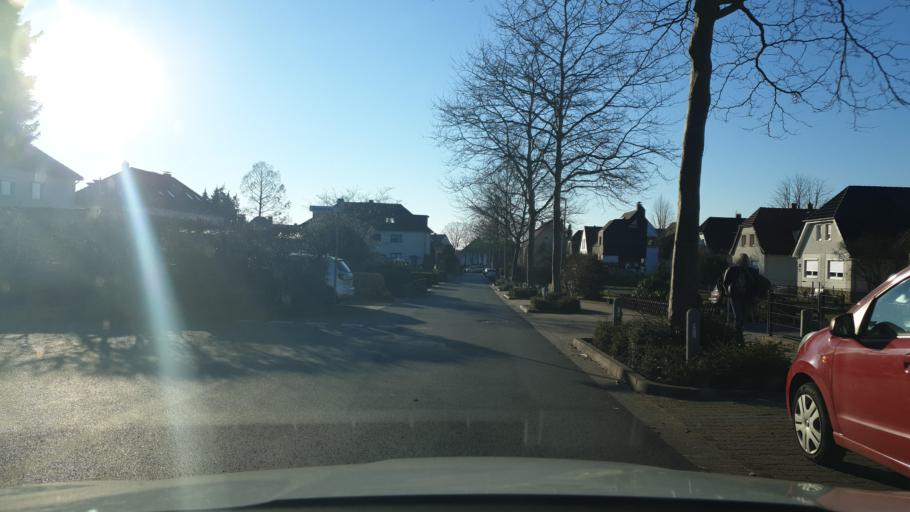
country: DE
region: North Rhine-Westphalia
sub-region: Regierungsbezirk Detmold
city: Herford
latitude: 52.1237
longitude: 8.6963
